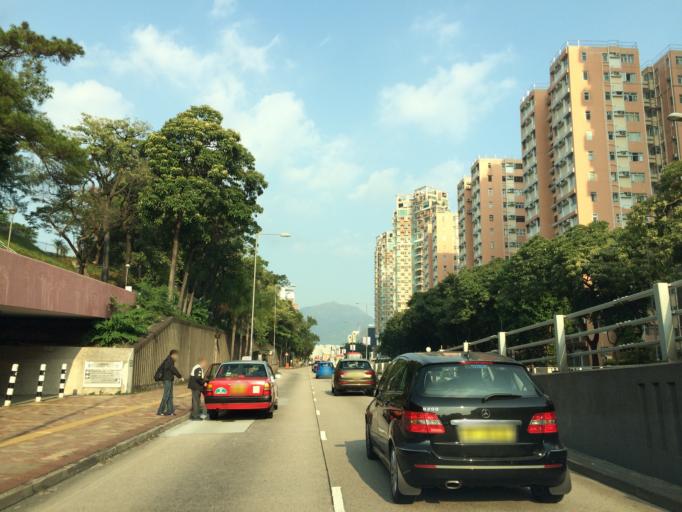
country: HK
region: Kowloon City
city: Kowloon
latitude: 22.3223
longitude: 114.1796
